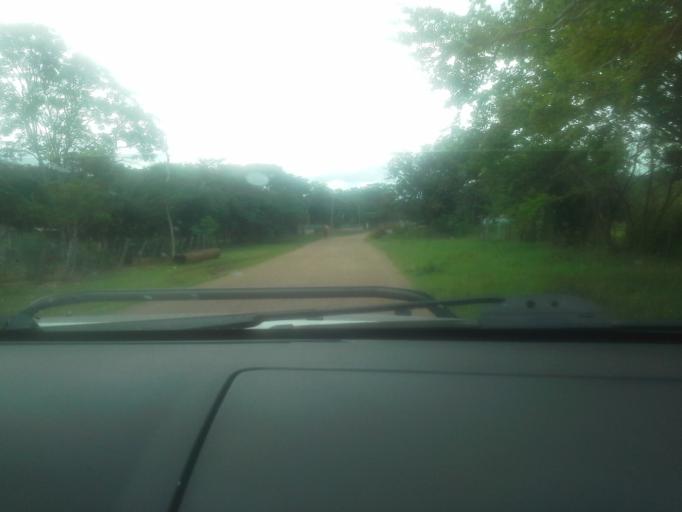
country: NI
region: Matagalpa
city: Ciudad Dario
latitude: 12.8183
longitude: -86.1928
